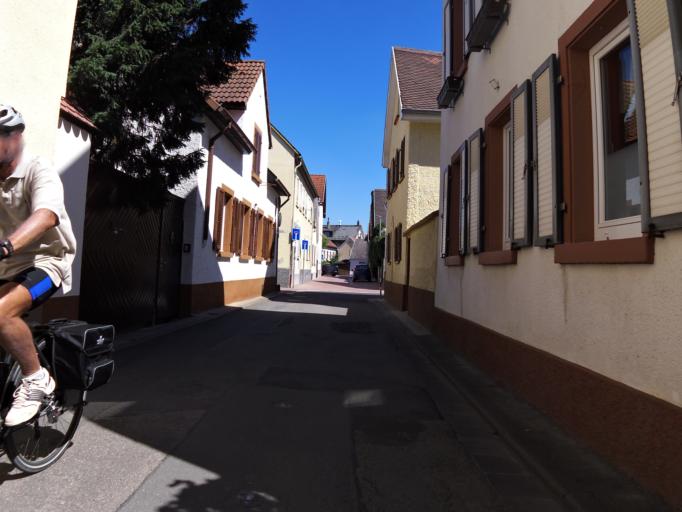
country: DE
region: Rheinland-Pfalz
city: Nierstein
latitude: 49.8739
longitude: 8.3383
